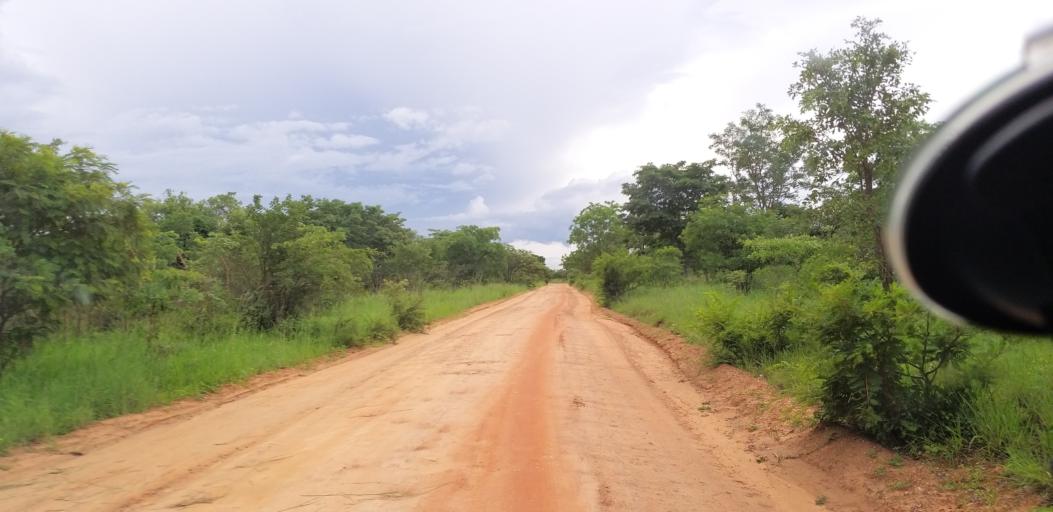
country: ZM
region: Lusaka
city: Chongwe
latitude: -15.1580
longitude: 28.4980
